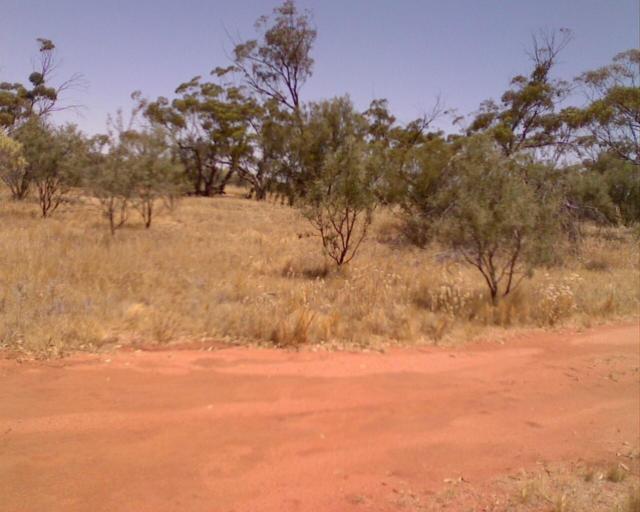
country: AU
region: Western Australia
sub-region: Merredin
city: Merredin
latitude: -30.8401
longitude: 117.9021
